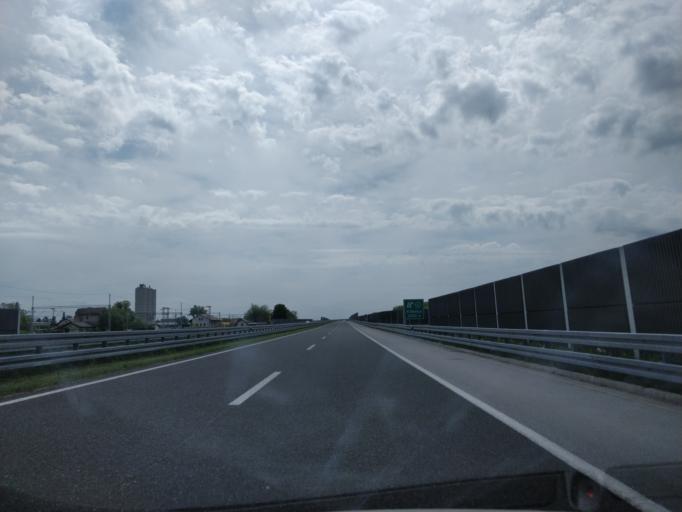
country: HR
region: Zagrebacka
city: Gradici
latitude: 45.7105
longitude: 16.0429
